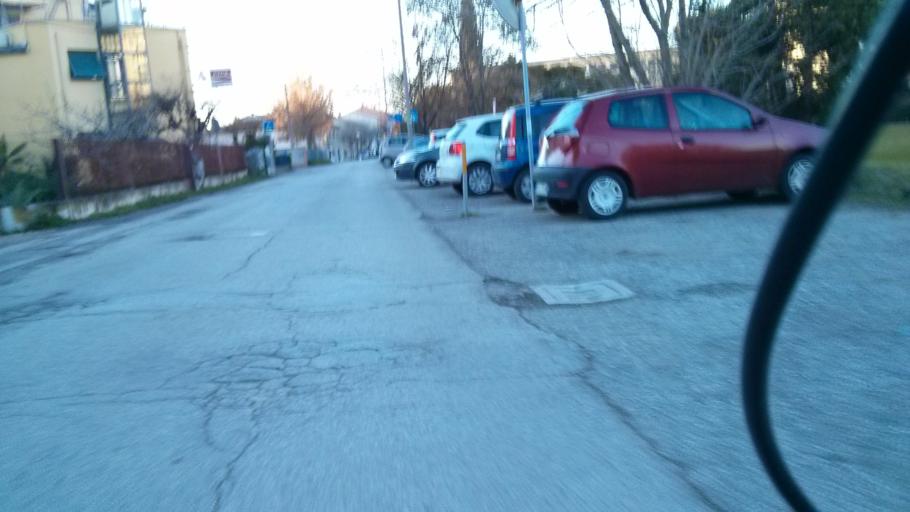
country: IT
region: The Marches
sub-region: Provincia di Pesaro e Urbino
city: Fano
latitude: 43.8346
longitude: 13.0256
